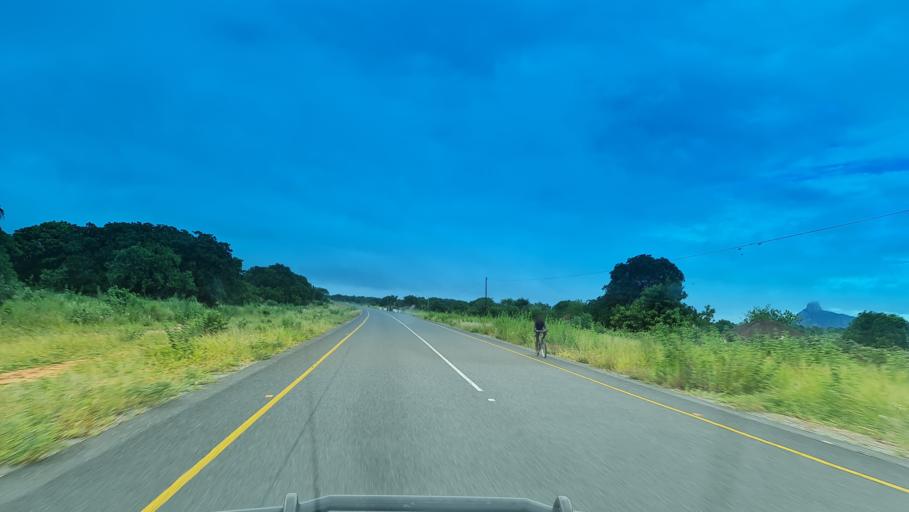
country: MZ
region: Nampula
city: Nampula
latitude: -15.5786
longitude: 39.3235
